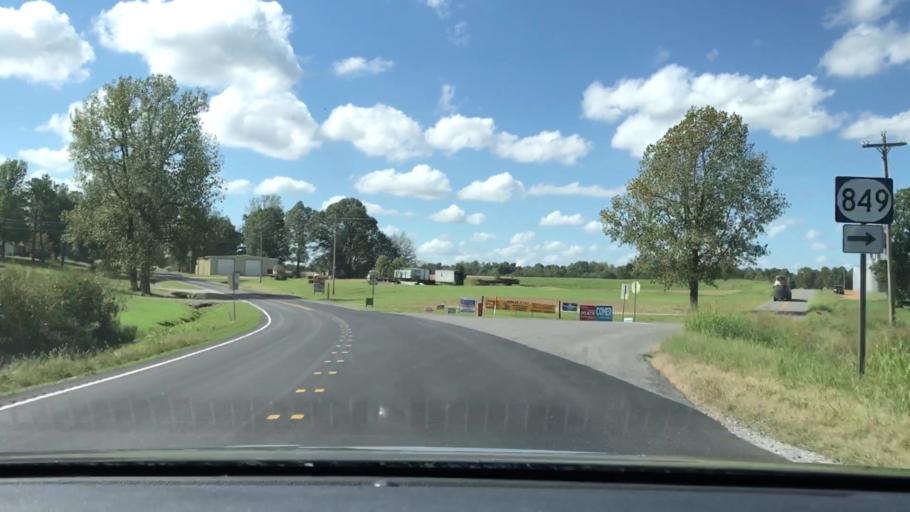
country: US
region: Kentucky
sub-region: McCracken County
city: Reidland
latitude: 36.8840
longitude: -88.5542
